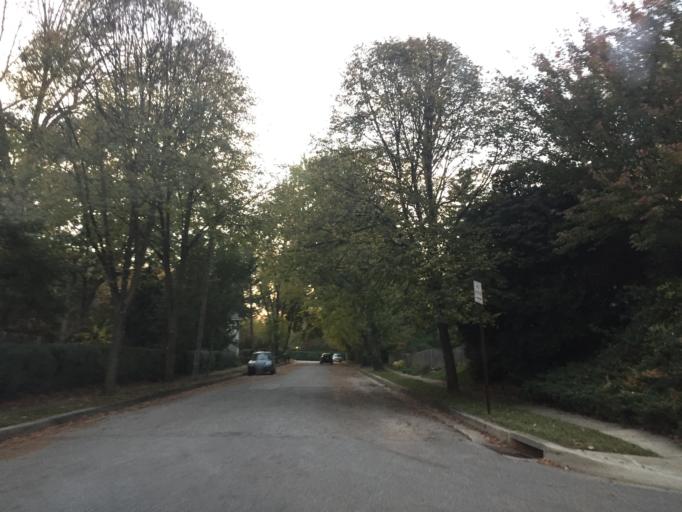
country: US
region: Maryland
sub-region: Baltimore County
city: Towson
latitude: 39.3521
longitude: -76.6307
